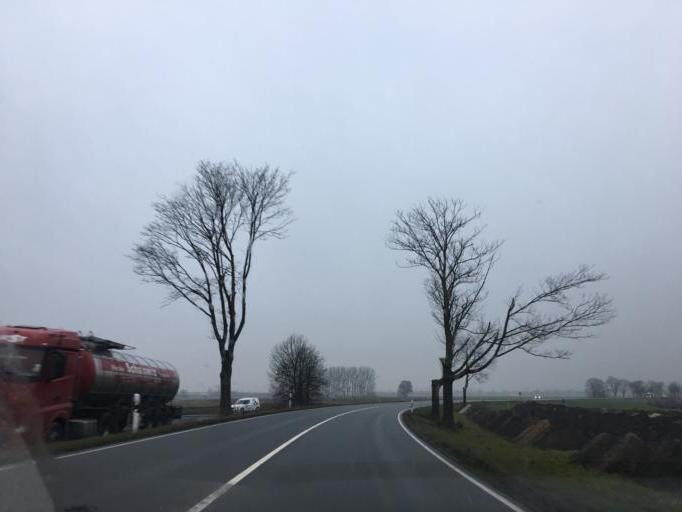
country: DE
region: Saxony-Anhalt
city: Gross Ammensleben
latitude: 52.2593
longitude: 11.4819
